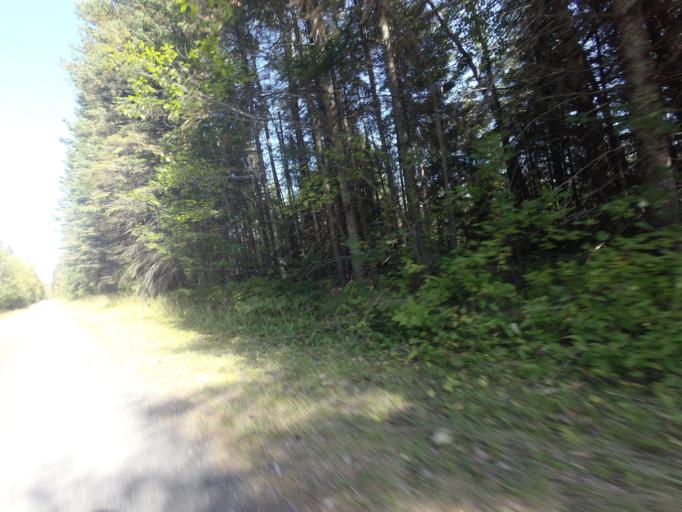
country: CA
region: Quebec
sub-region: Laurentides
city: Sainte-Agathe-des-Monts
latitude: 46.0692
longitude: -74.3141
